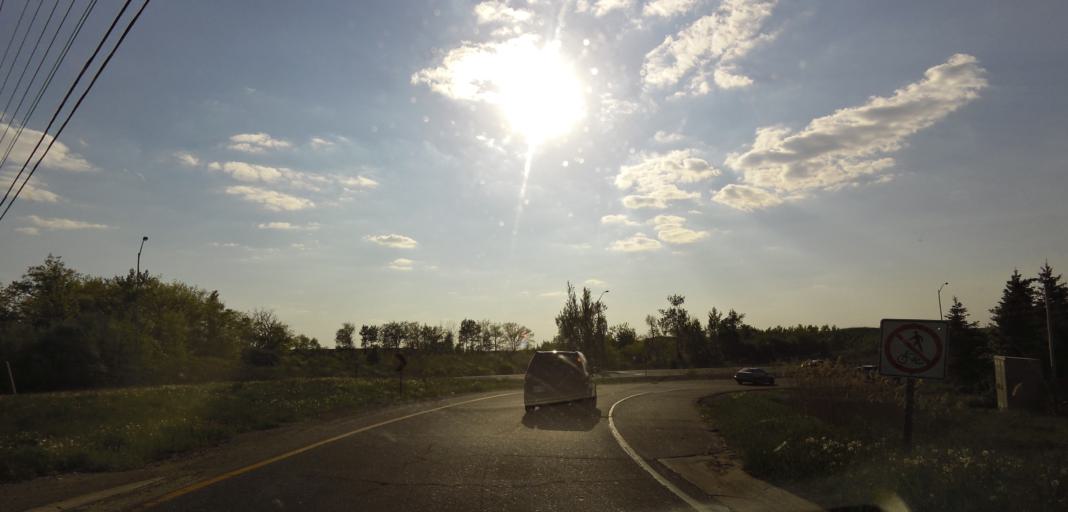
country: CA
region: Ontario
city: Brampton
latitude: 43.7251
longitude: -79.7663
